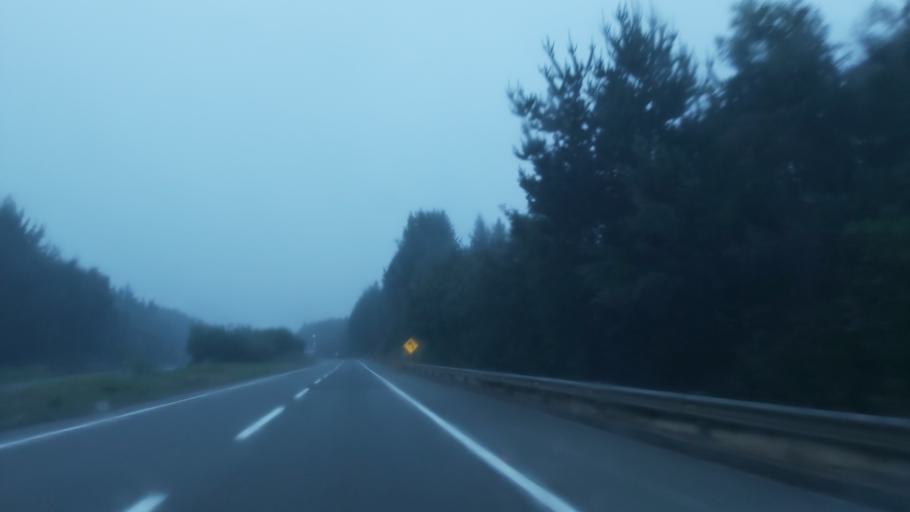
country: CL
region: Biobio
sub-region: Provincia de Concepcion
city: Penco
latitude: -36.7445
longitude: -72.9150
